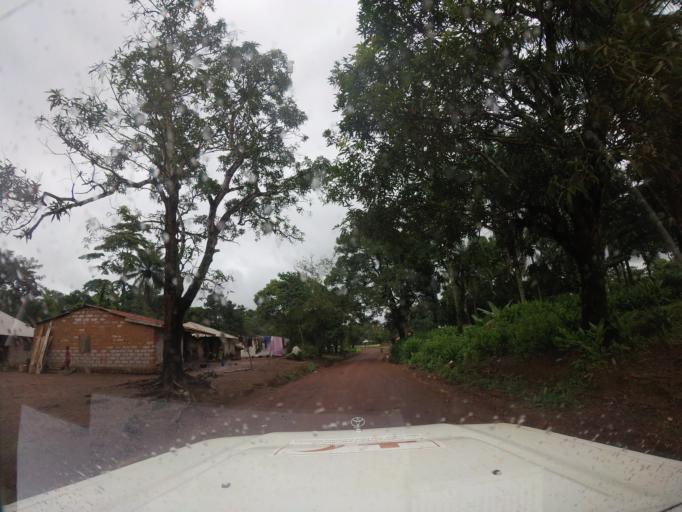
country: SL
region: Northern Province
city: Kambia
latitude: 9.1301
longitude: -12.8887
